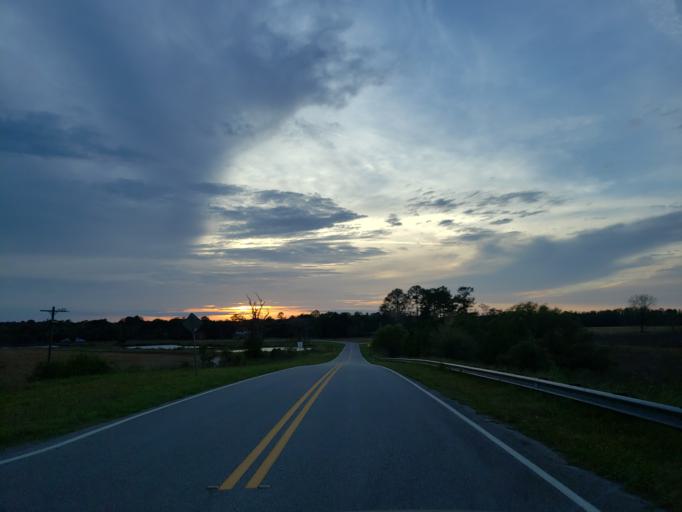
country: US
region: Georgia
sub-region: Lowndes County
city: Hahira
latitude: 30.9500
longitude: -83.3759
